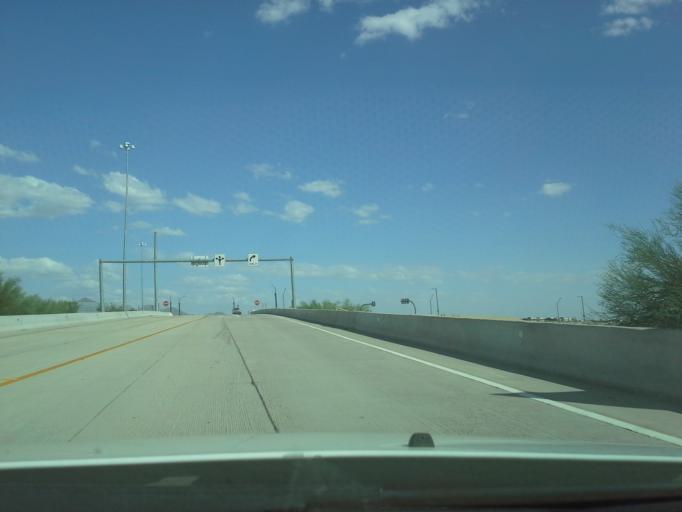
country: US
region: Arizona
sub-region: Maricopa County
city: Paradise Valley
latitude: 33.6618
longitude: -111.9446
